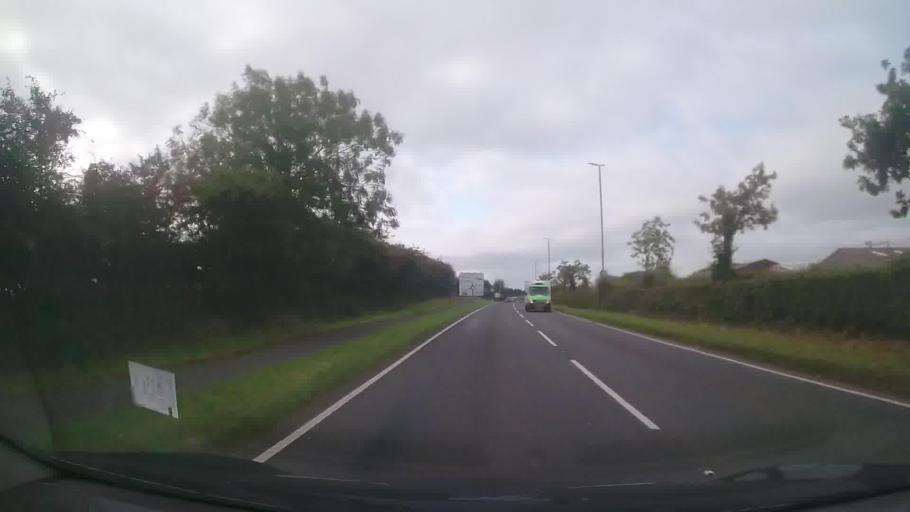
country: GB
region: Wales
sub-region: Pembrokeshire
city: Neyland
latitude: 51.7171
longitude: -4.9513
